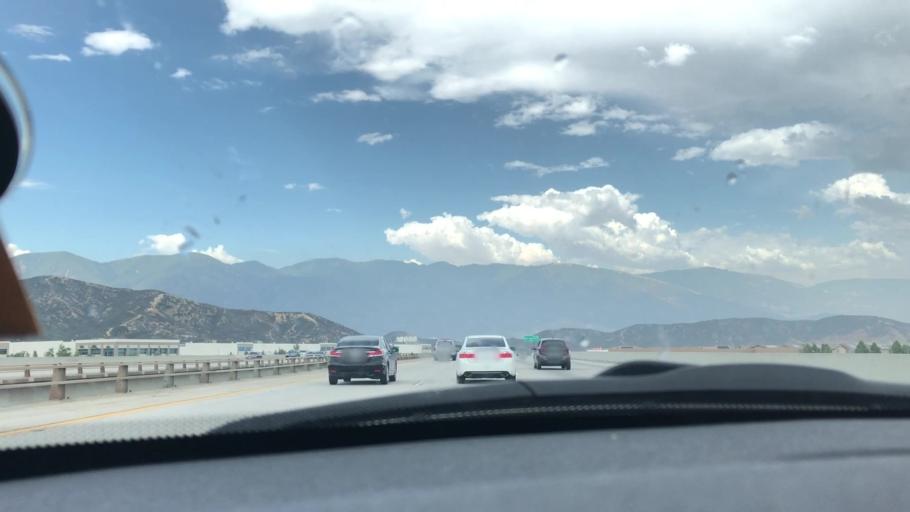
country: US
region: California
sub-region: San Bernardino County
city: Fontana
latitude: 34.1855
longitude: -117.4321
